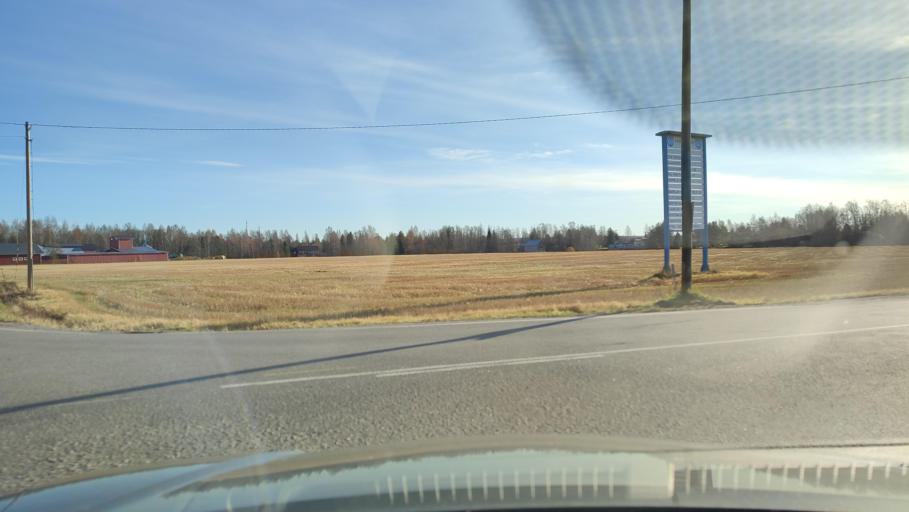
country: FI
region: Southern Ostrobothnia
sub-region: Suupohja
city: Teuva
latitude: 62.4749
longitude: 21.7153
